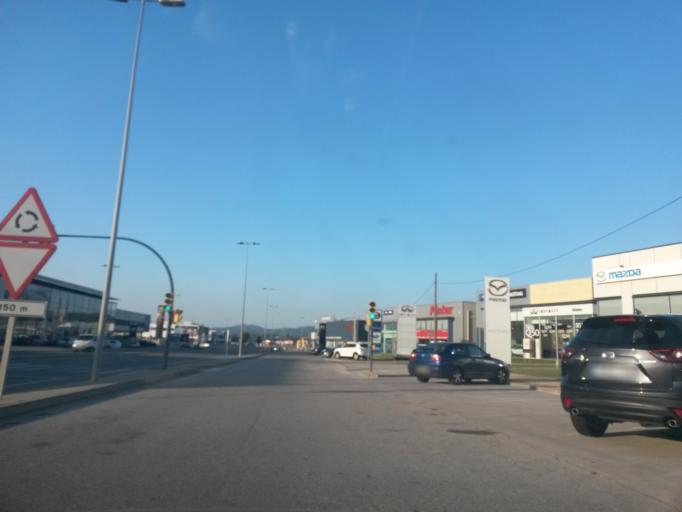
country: ES
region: Catalonia
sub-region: Provincia de Girona
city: Fornells de la Selva
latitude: 41.9341
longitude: 2.7970
